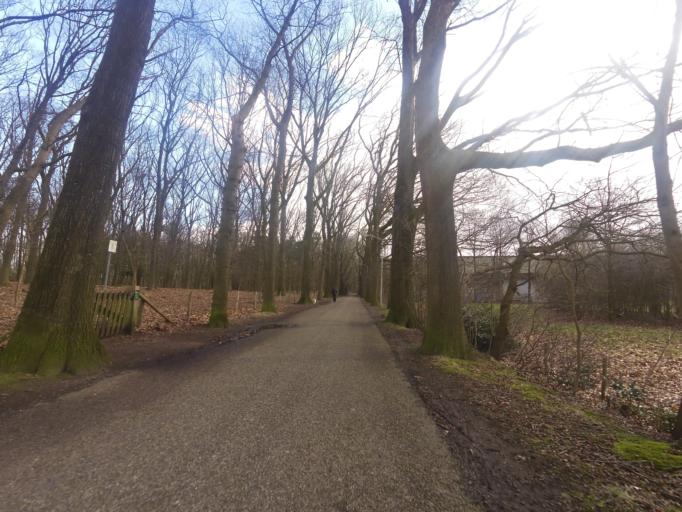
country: NL
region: Gelderland
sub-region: Gemeente Doetinchem
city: Doetinchem
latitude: 51.9570
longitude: 6.3089
